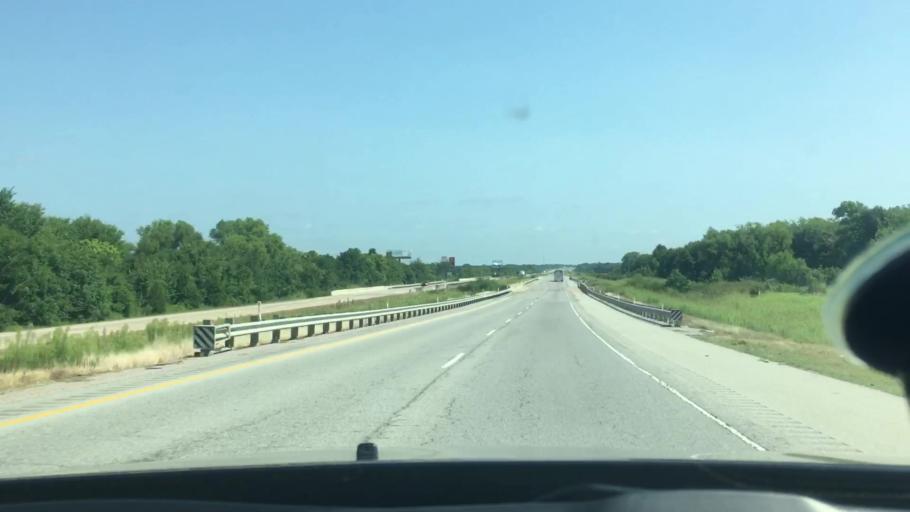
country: US
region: Oklahoma
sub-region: Atoka County
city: Atoka
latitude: 34.2397
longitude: -96.2201
